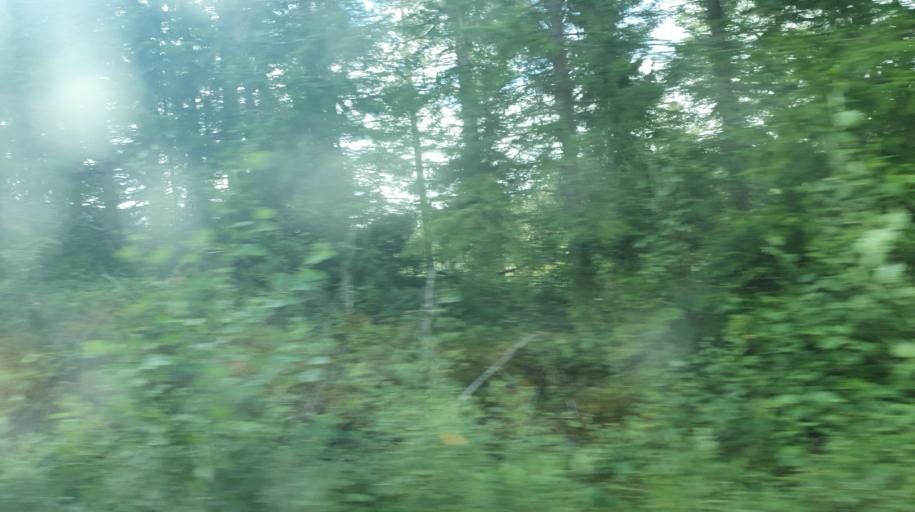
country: NO
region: Nord-Trondelag
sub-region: Levanger
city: Skogn
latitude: 63.5819
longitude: 11.2463
